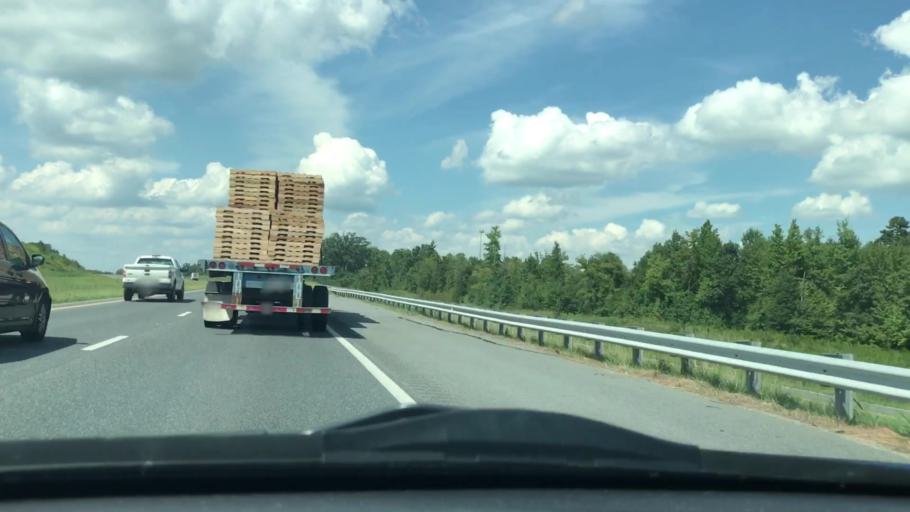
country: US
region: North Carolina
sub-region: Randolph County
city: Randleman
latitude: 35.8398
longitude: -79.8632
